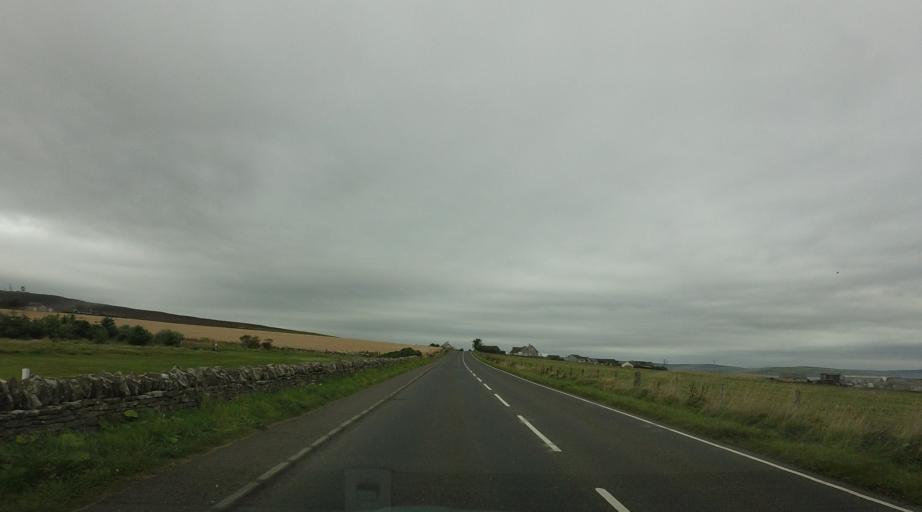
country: GB
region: Scotland
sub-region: Orkney Islands
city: Orkney
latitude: 58.9892
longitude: -2.9857
